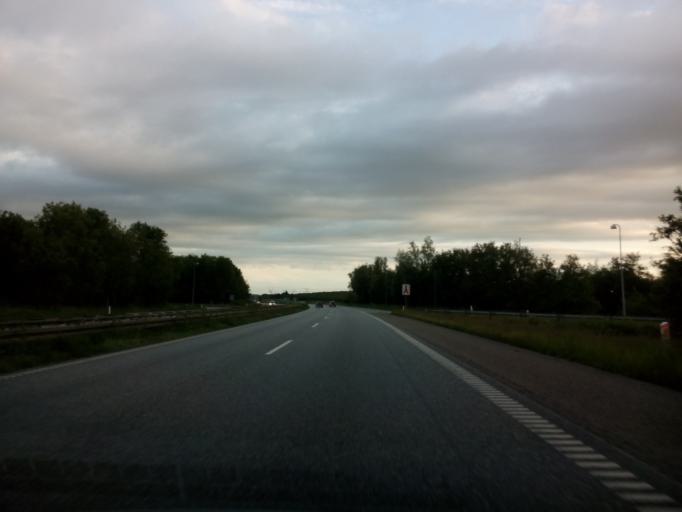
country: DK
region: North Denmark
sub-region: Alborg Kommune
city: Aalborg
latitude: 57.0065
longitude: 9.9120
